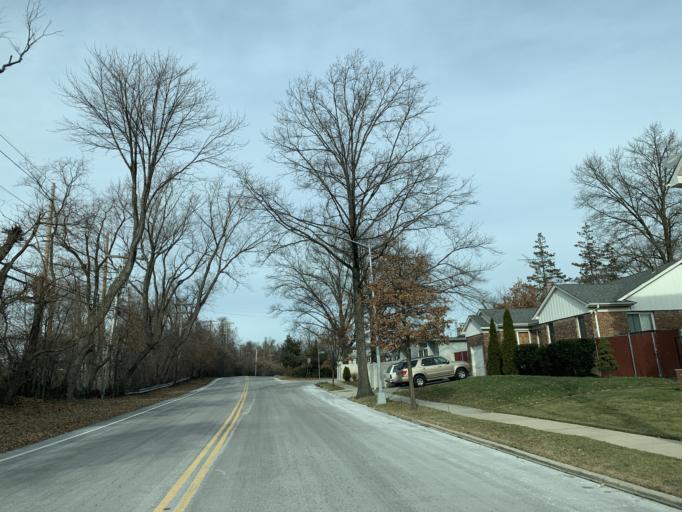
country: US
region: New York
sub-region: Nassau County
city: Lake Success
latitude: 40.7515
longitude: -73.7285
